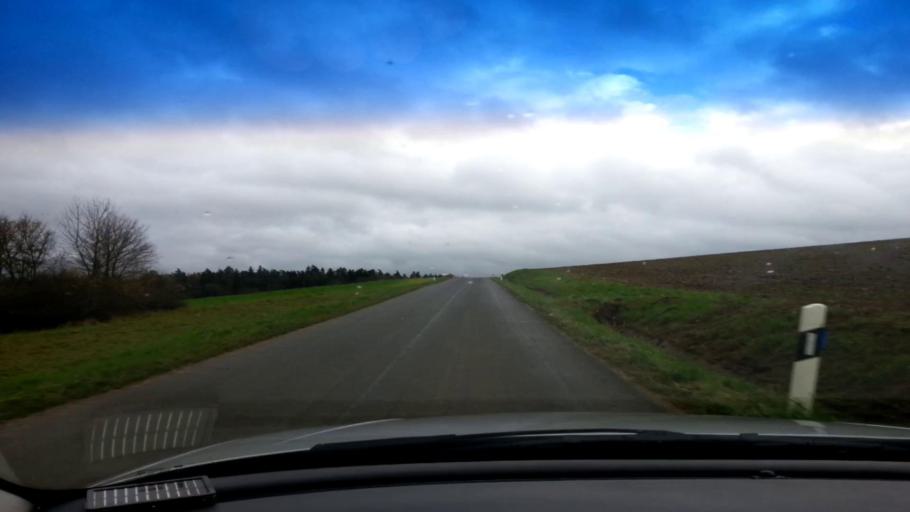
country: DE
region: Bavaria
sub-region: Upper Franconia
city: Zapfendorf
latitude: 50.0277
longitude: 10.9682
